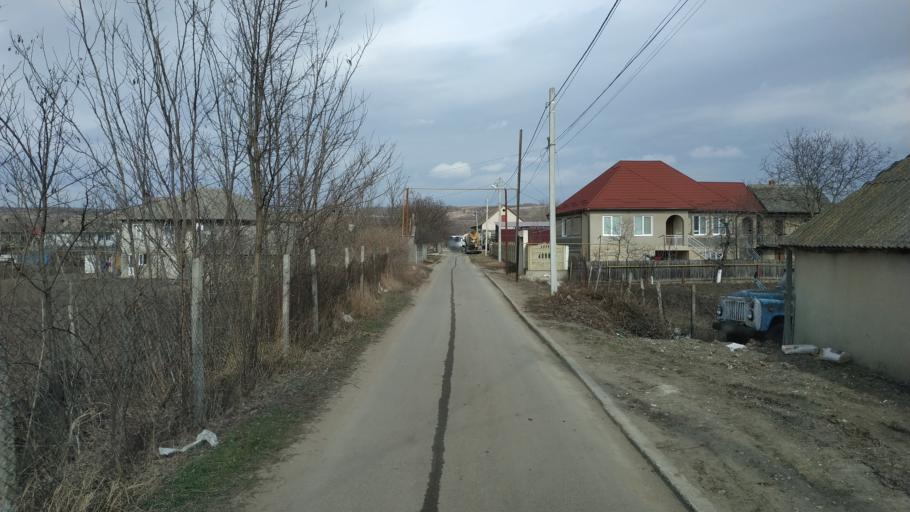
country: MD
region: Laloveni
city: Ialoveni
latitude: 46.8628
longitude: 28.7807
